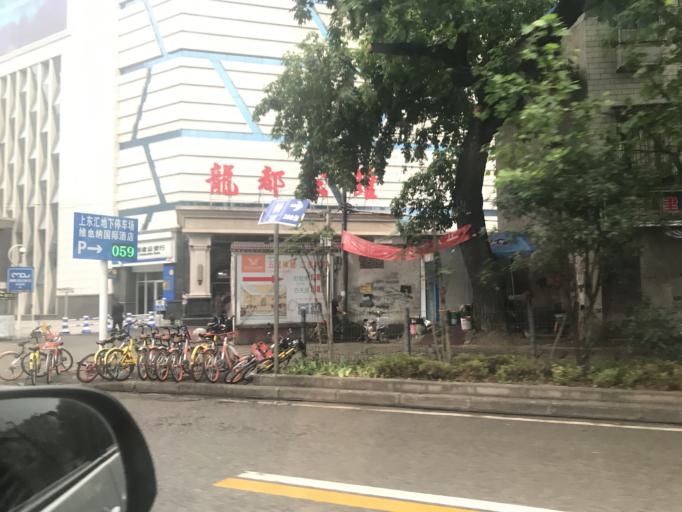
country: CN
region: Hubei
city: Jiang'an
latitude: 30.6173
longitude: 114.3059
